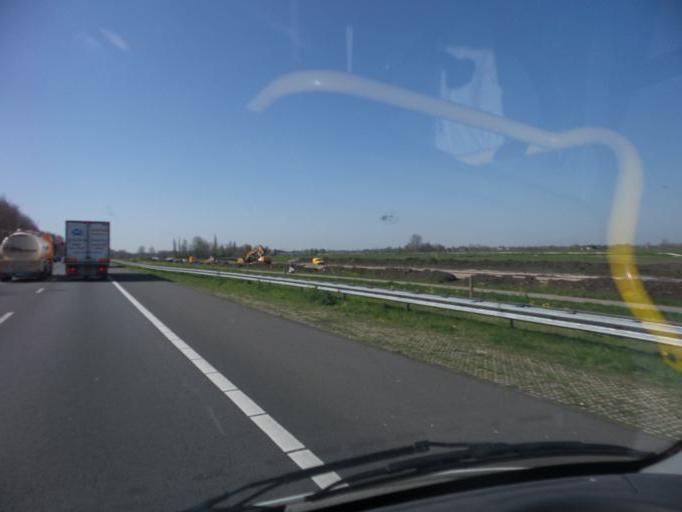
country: NL
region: South Holland
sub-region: Bodegraven-Reeuwijk
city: Reeuwijk
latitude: 52.0495
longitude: 4.7163
